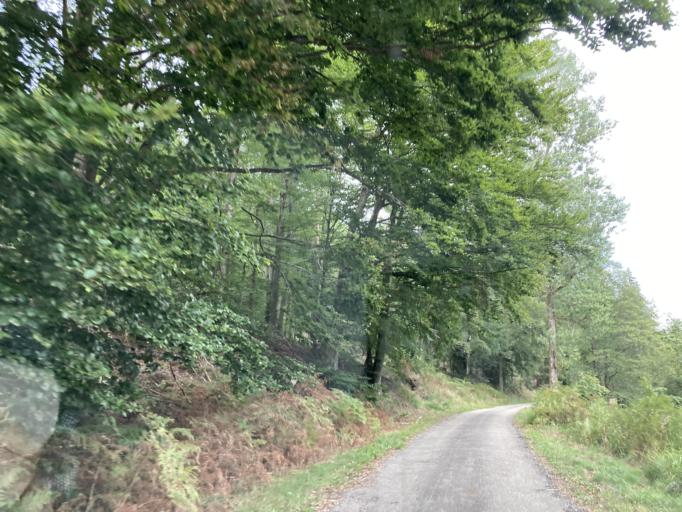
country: DE
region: Baden-Wuerttemberg
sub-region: Karlsruhe Region
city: Dobel
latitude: 48.7770
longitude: 8.5021
